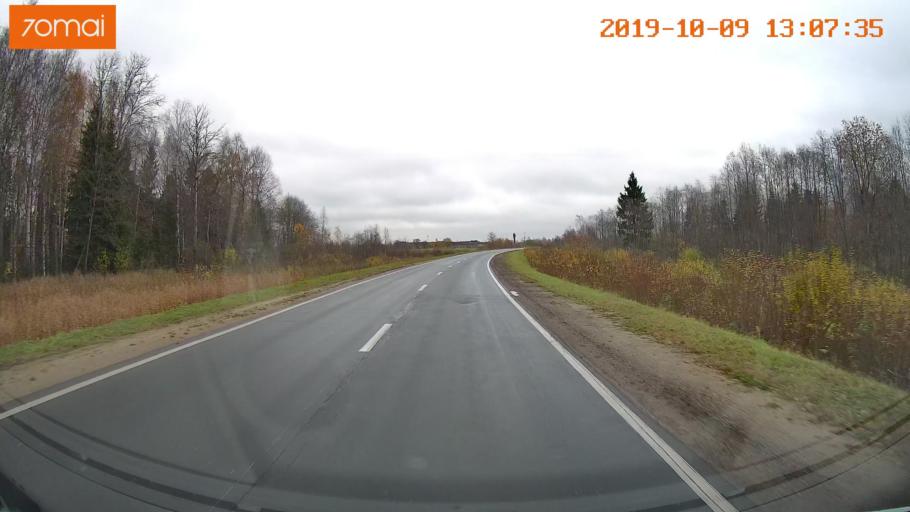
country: RU
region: Jaroslavl
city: Lyubim
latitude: 58.3569
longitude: 40.6461
